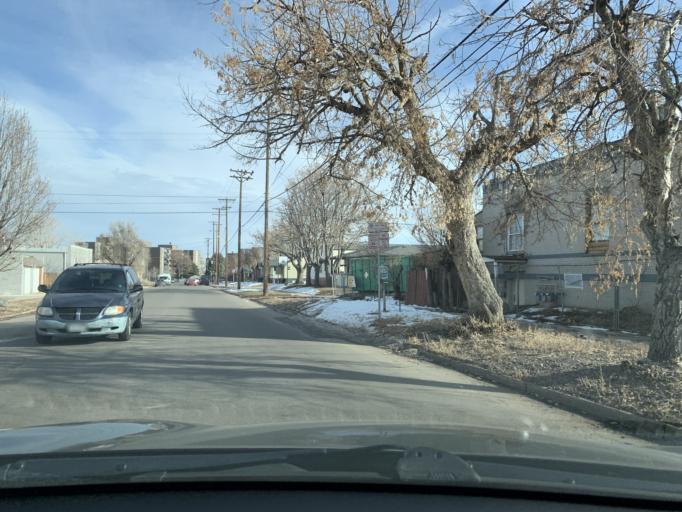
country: US
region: Colorado
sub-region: Jefferson County
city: Edgewater
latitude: 39.7385
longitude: -105.0322
